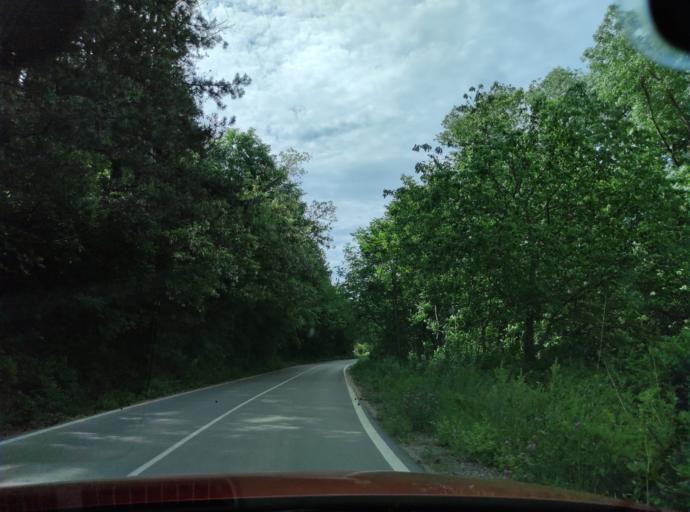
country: BG
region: Montana
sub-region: Obshtina Chiprovtsi
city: Chiprovtsi
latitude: 43.4420
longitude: 22.9346
